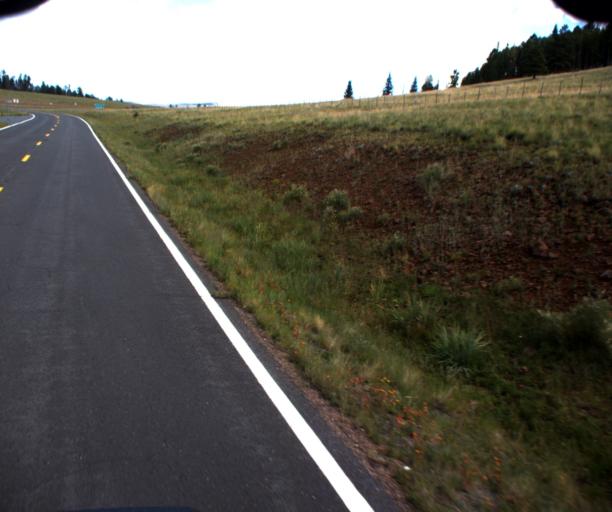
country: US
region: Arizona
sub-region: Apache County
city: Eagar
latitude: 33.9092
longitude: -109.4141
